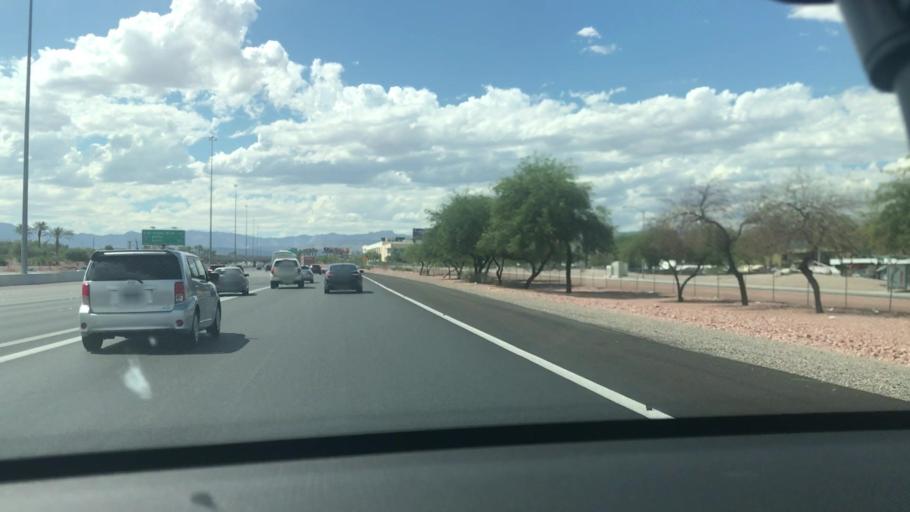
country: US
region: Nevada
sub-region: Clark County
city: Paradise
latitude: 36.0642
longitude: -115.1552
